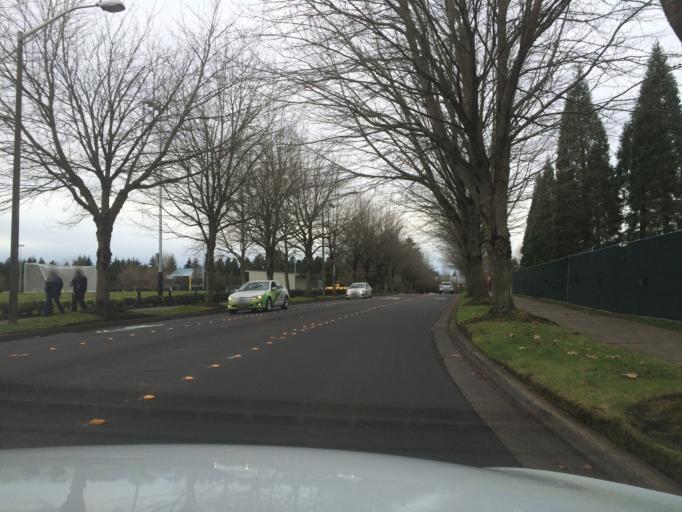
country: US
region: Washington
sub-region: King County
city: Redmond
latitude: 47.6425
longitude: -122.1279
